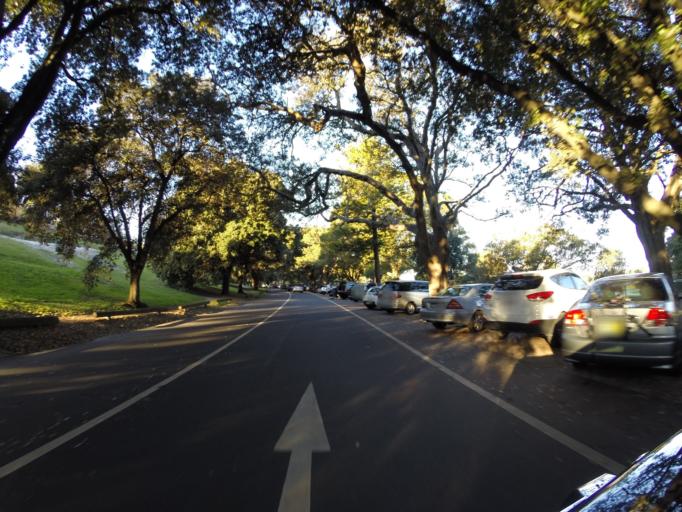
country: AU
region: New South Wales
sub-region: Woollahra
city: Woollahra
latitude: -33.8974
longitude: 151.2282
